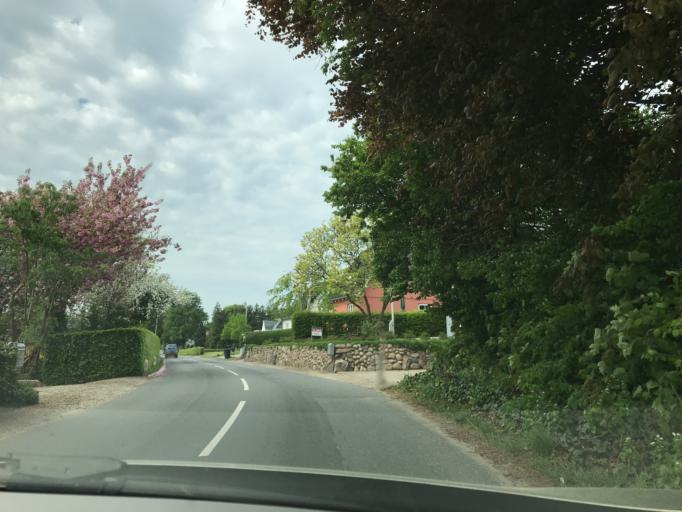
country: DK
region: South Denmark
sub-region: Assens Kommune
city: Assens
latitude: 55.3270
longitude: 9.9346
